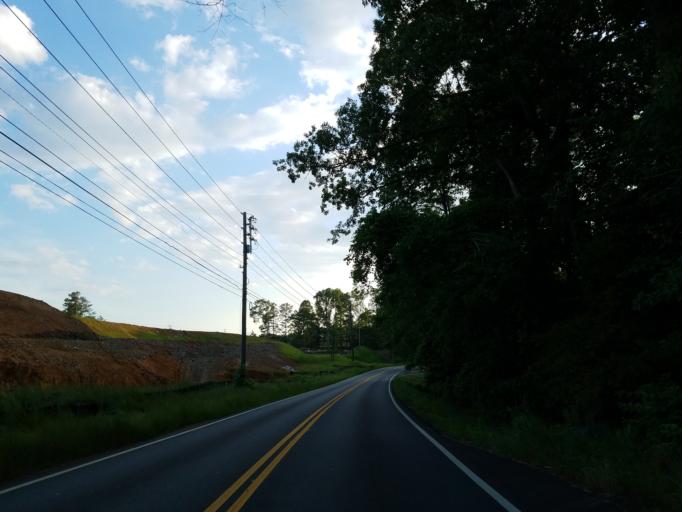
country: US
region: Georgia
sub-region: Cherokee County
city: Holly Springs
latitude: 34.1755
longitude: -84.5539
